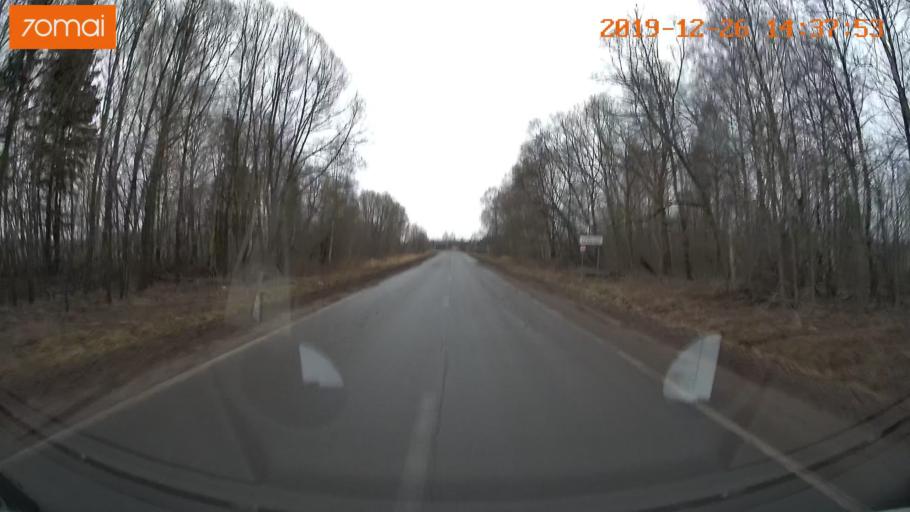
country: RU
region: Jaroslavl
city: Poshekhon'ye
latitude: 58.3987
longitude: 38.9716
